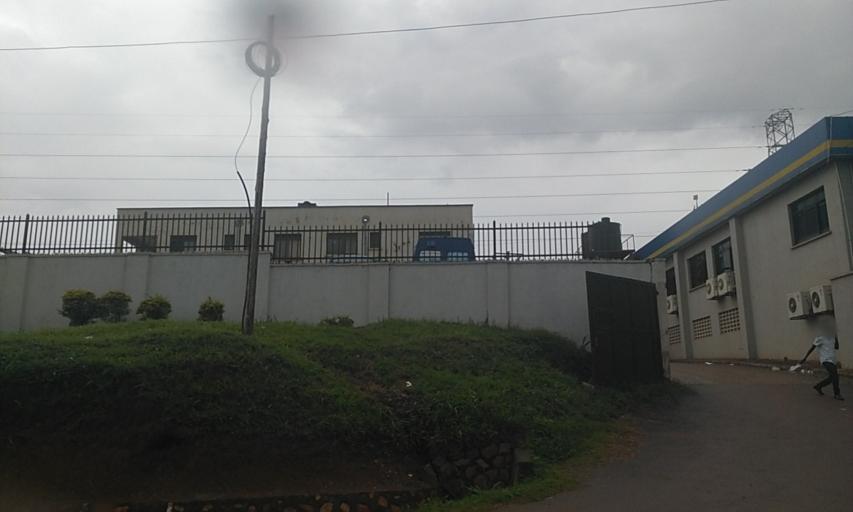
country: UG
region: Central Region
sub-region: Wakiso District
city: Kireka
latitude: 0.3360
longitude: 32.6204
